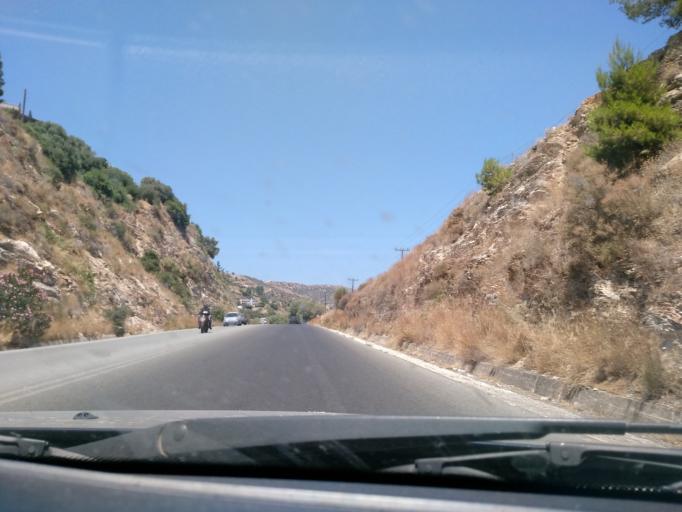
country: GR
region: Crete
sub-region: Nomos Irakleiou
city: Gazi
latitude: 35.3557
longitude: 25.0401
